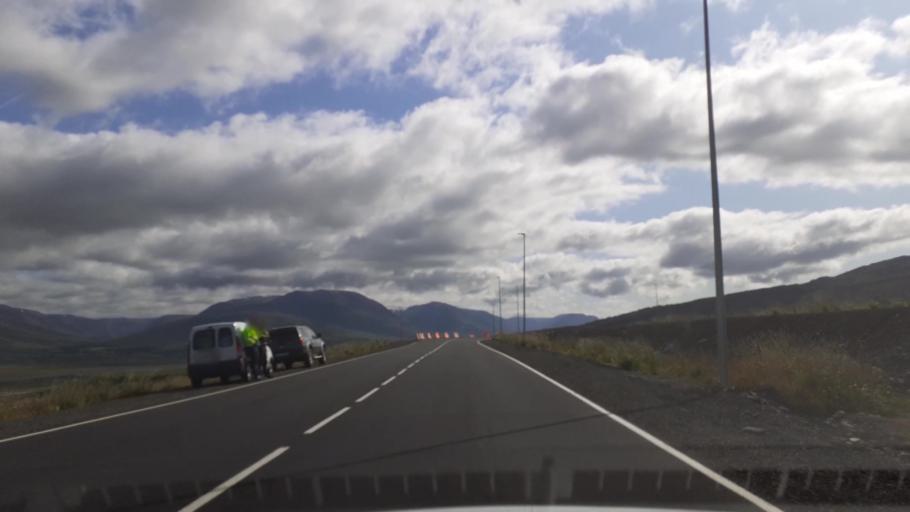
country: IS
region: Northeast
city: Akureyri
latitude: 65.6579
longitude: -18.0889
